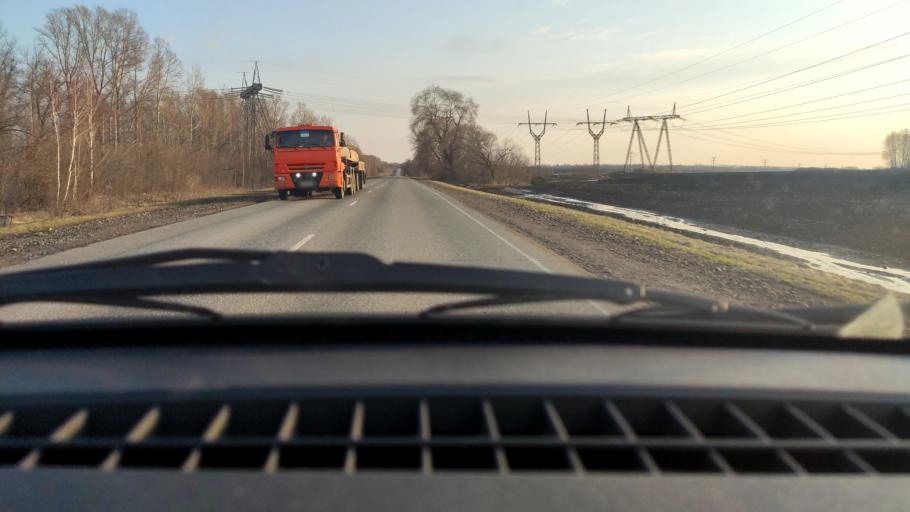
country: RU
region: Bashkortostan
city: Chishmy
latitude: 54.5196
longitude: 55.2973
